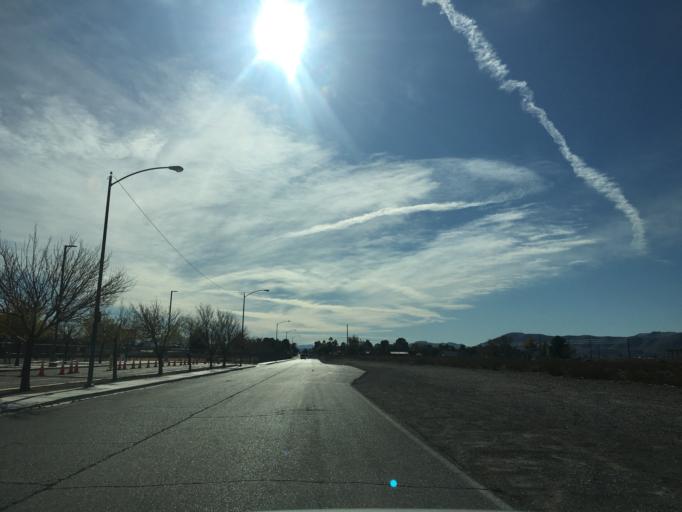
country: US
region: Nevada
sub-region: Clark County
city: Enterprise
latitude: 36.0018
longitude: -115.1682
